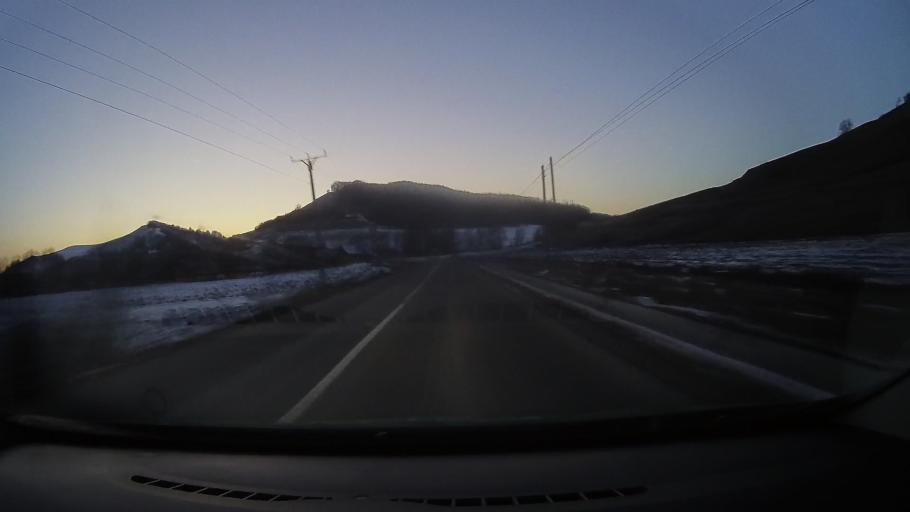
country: RO
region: Sibiu
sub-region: Comuna Alma
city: Alma
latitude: 46.2042
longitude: 24.4557
